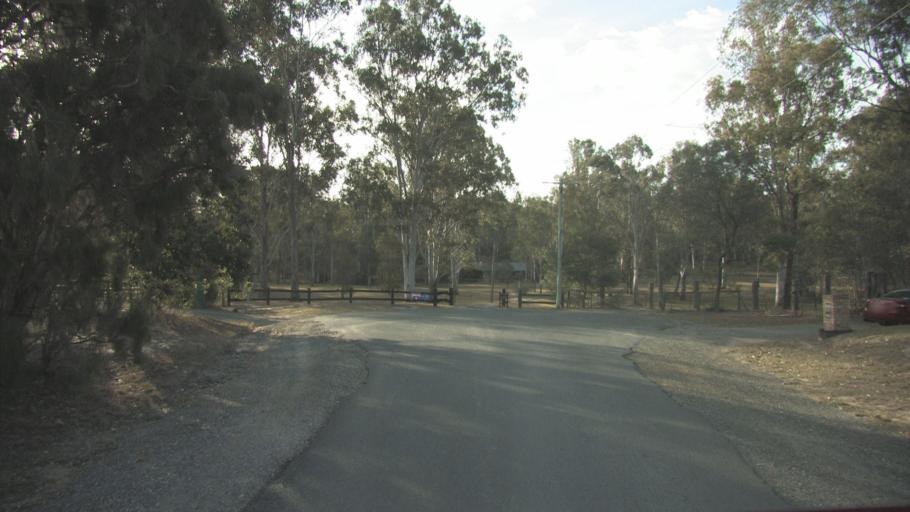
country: AU
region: Queensland
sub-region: Logan
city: Cedar Vale
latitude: -27.8538
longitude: 153.0615
